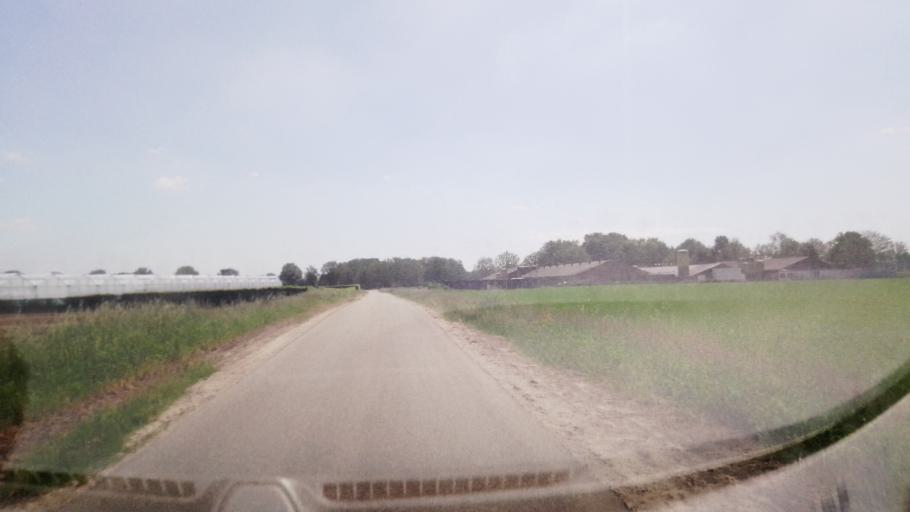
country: NL
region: Limburg
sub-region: Gemeente Beesel
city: Beesel
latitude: 51.3065
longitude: 6.0379
